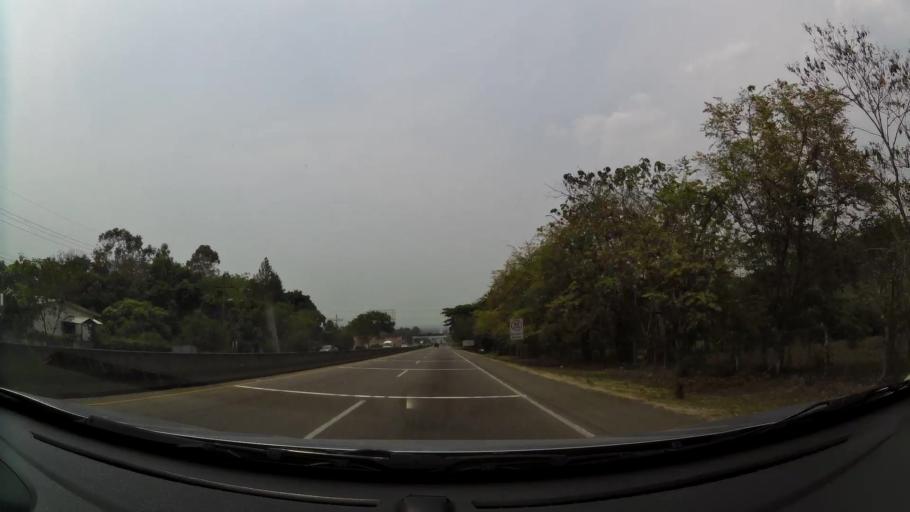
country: HN
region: Cortes
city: Oropendolas
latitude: 15.0274
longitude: -87.9277
